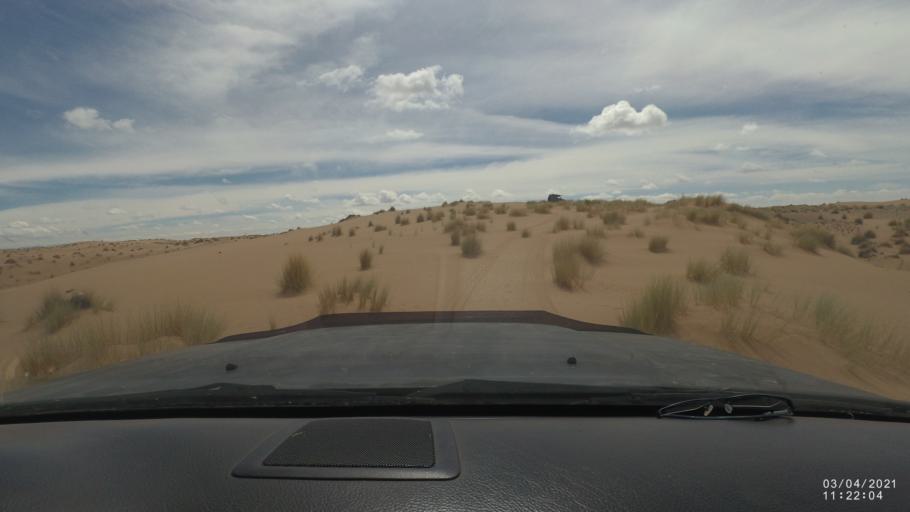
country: BO
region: Oruro
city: Poopo
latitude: -18.7040
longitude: -67.5127
